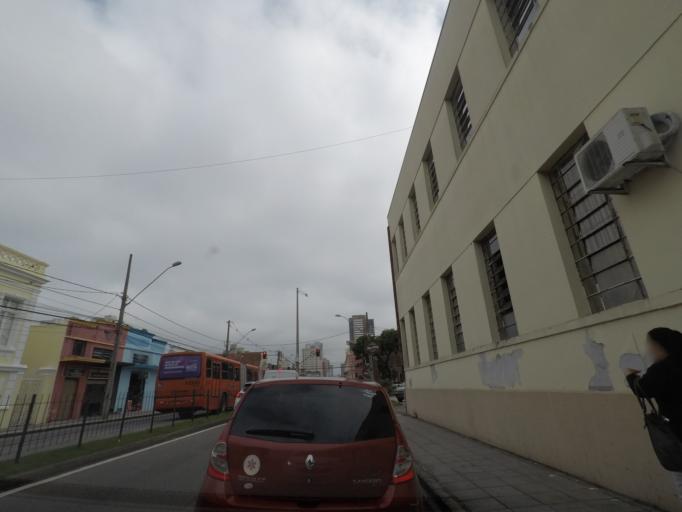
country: BR
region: Parana
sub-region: Curitiba
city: Curitiba
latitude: -25.4418
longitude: -49.2666
